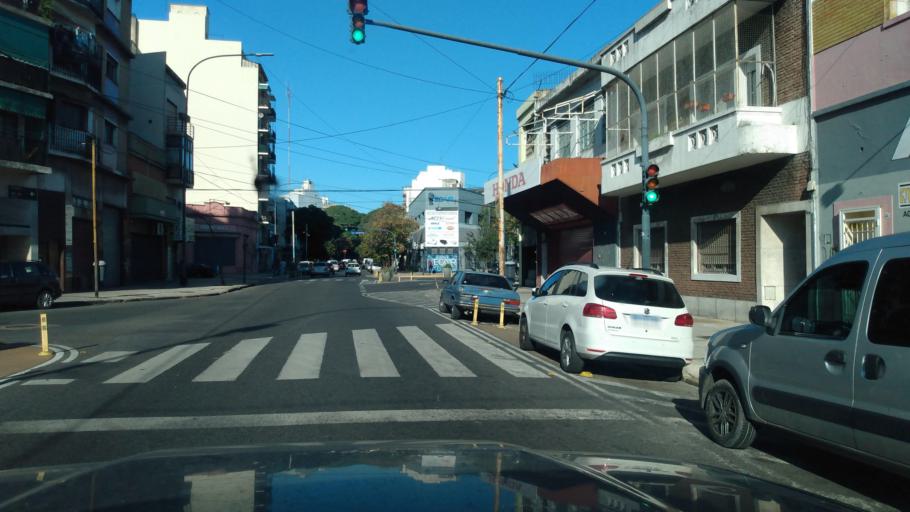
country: AR
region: Buenos Aires F.D.
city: Colegiales
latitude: -34.6012
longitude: -58.4453
